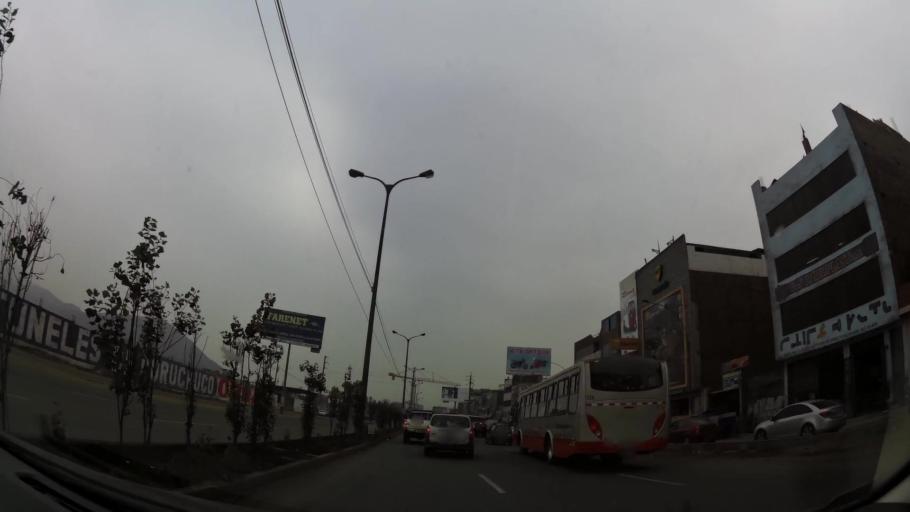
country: PE
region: Lima
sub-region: Lima
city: Vitarte
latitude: -12.0394
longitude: -76.9330
